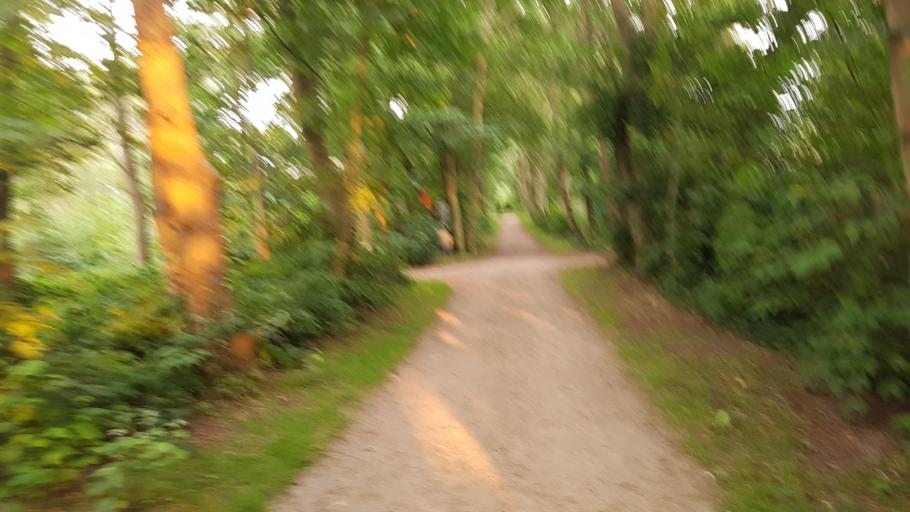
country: DE
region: Schleswig-Holstein
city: Sankt Peter-Ording
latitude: 54.3004
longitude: 8.6464
